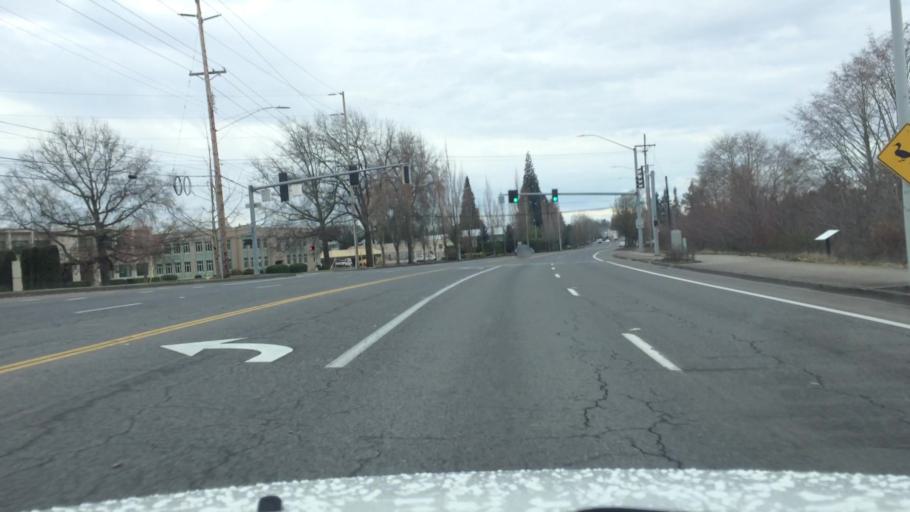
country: US
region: Oregon
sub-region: Marion County
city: Four Corners
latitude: 44.9289
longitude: -123.0028
